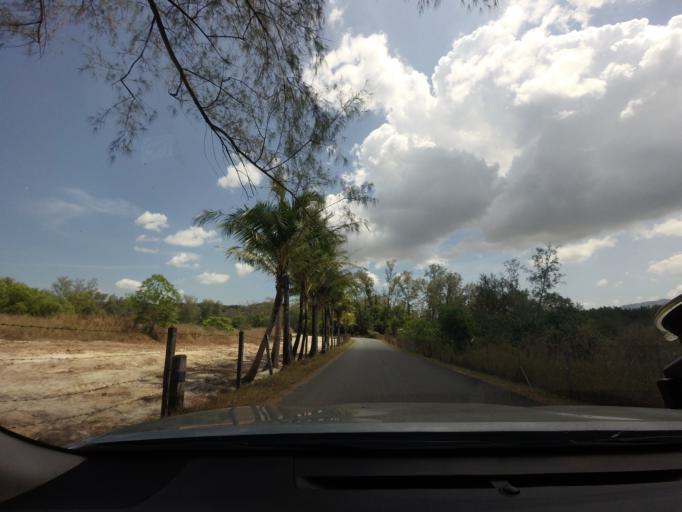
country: TH
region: Phuket
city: Thalang
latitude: 8.0333
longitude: 98.2896
